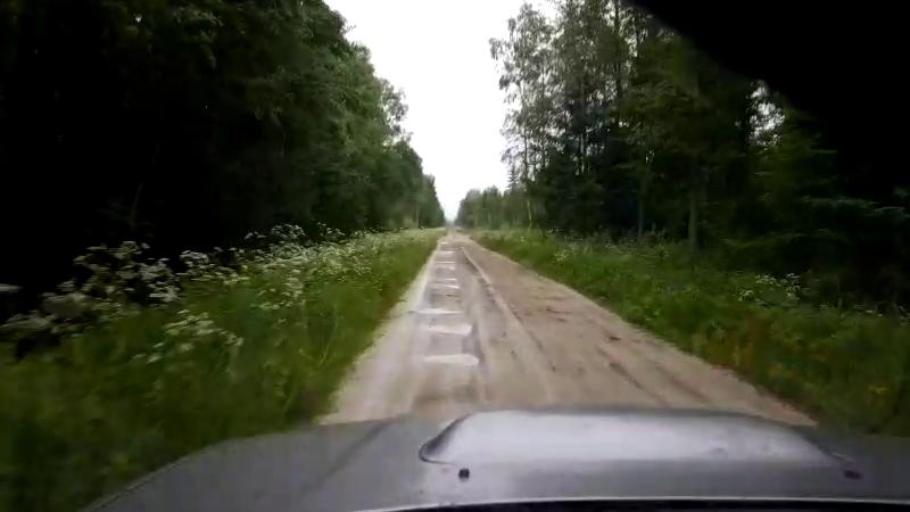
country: EE
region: Paernumaa
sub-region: Halinga vald
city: Parnu-Jaagupi
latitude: 58.5817
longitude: 24.6380
